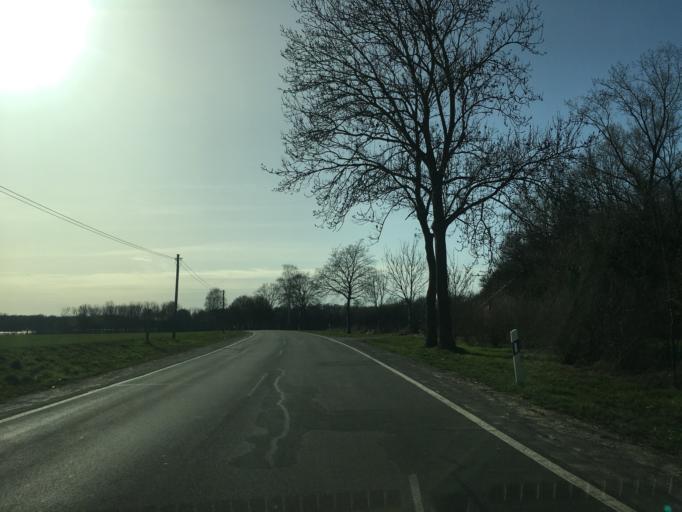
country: DE
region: North Rhine-Westphalia
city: Selm
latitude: 51.7229
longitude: 7.4942
